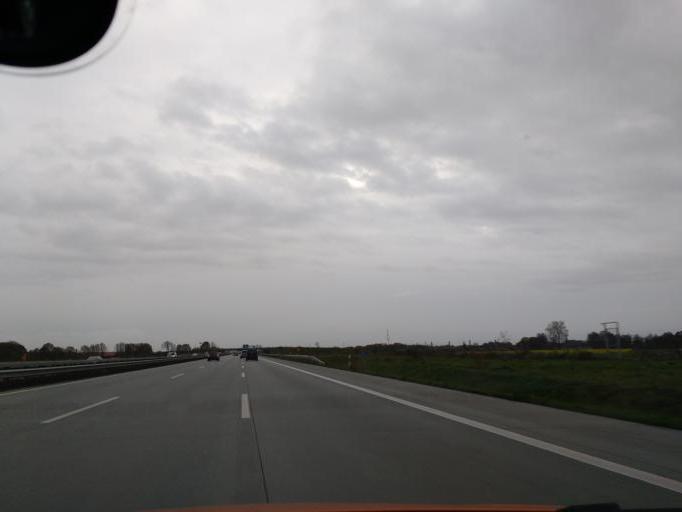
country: DE
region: Lower Saxony
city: Reessum
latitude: 53.1244
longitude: 9.2125
